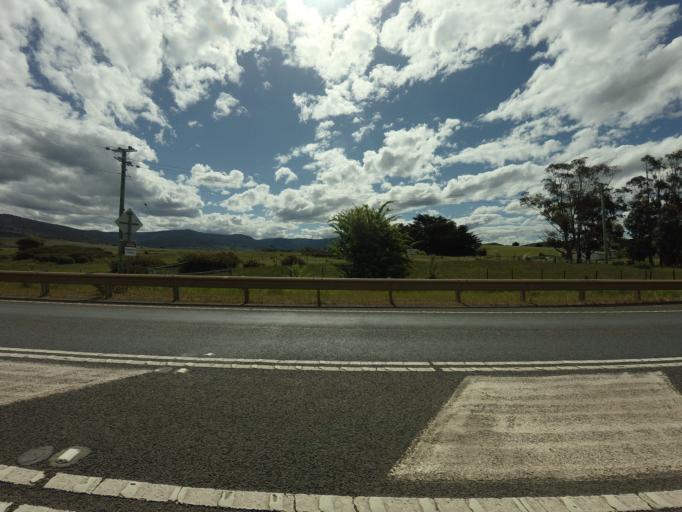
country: AU
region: Tasmania
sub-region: Brighton
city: Bridgewater
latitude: -42.1775
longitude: 147.3880
